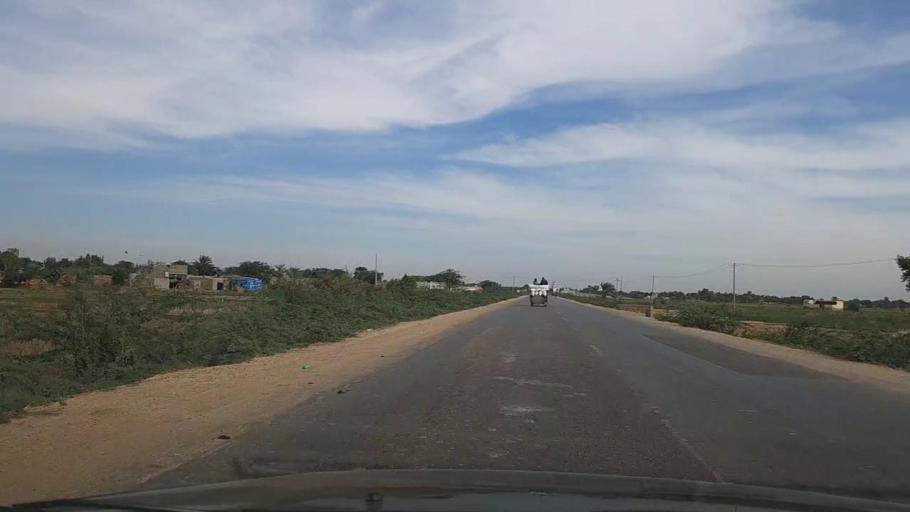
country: PK
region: Sindh
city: Thatta
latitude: 24.7784
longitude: 67.9464
